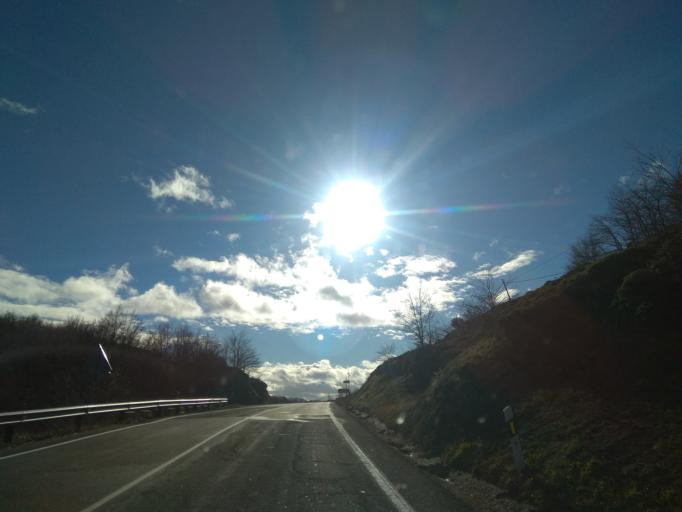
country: ES
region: Cantabria
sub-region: Provincia de Cantabria
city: San Martin de Elines
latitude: 42.9384
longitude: -3.8296
